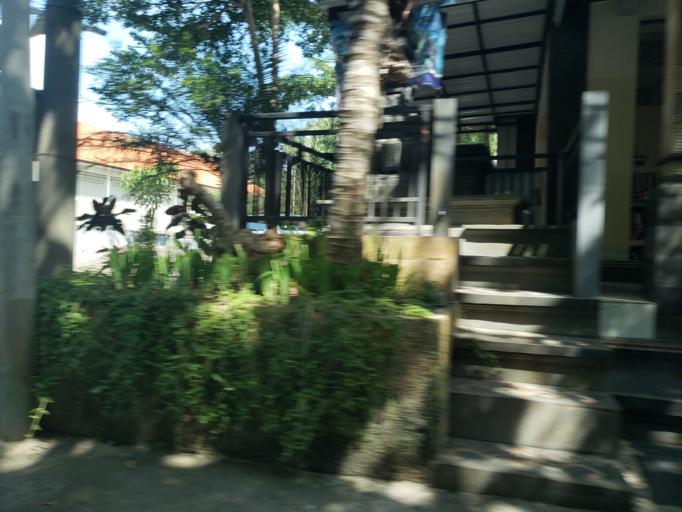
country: ID
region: Bali
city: Kangin
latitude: -8.8351
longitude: 115.1261
